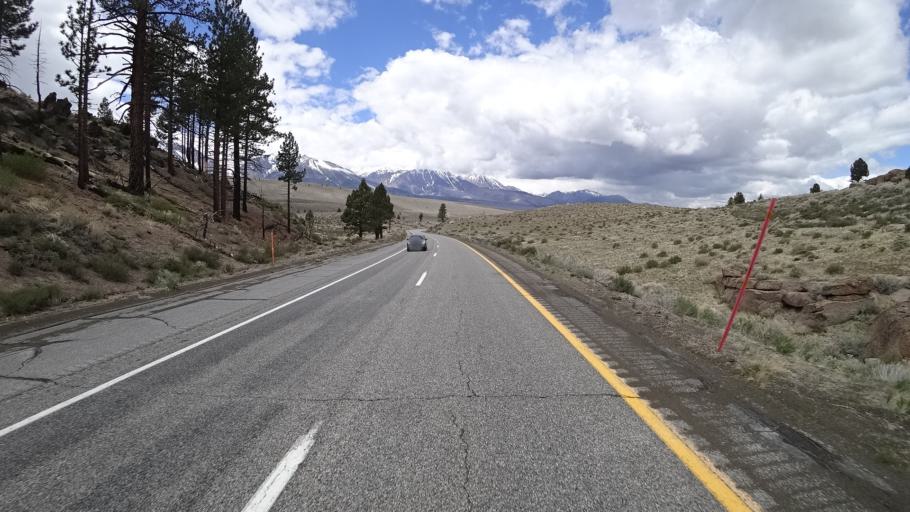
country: US
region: California
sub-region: Mono County
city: Mammoth Lakes
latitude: 37.8287
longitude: -119.0676
